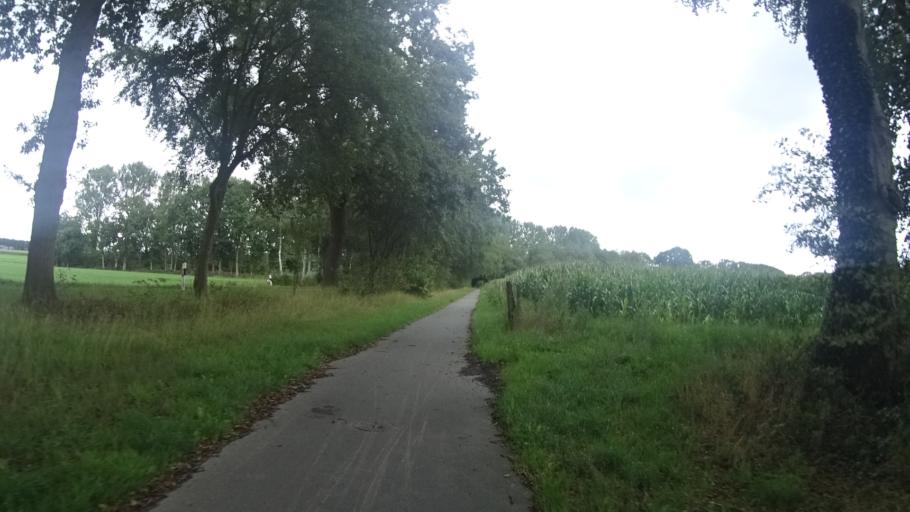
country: DE
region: Lower Saxony
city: Kuhrstedt
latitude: 53.5895
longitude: 8.8063
